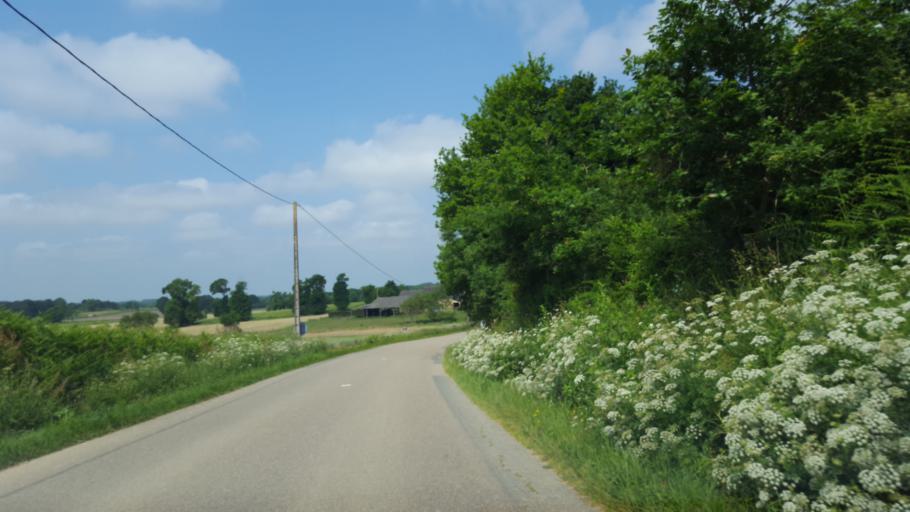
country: FR
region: Brittany
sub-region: Departement d'Ille-et-Vilaine
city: Guignen
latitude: 47.9223
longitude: -1.8796
